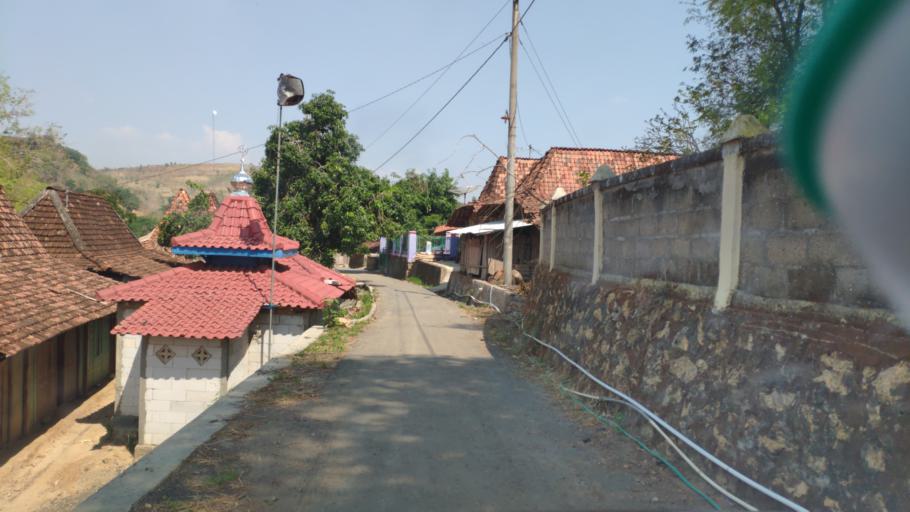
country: ID
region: Central Java
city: Koro
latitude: -6.9014
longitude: 111.1965
